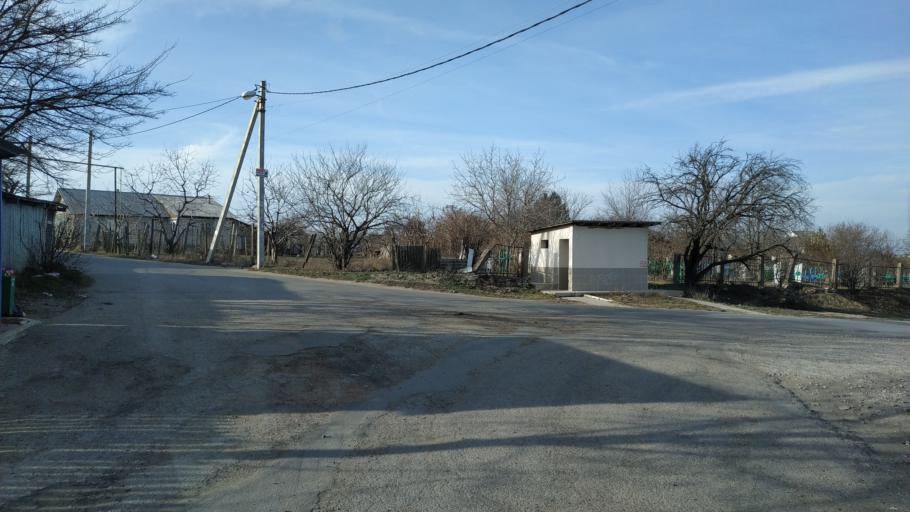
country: MD
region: Chisinau
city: Vatra
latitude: 47.0647
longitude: 28.6904
